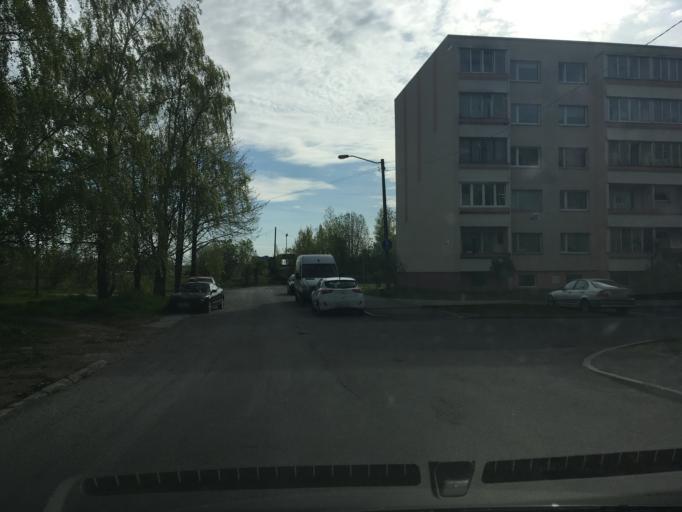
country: EE
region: Harju
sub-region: Tallinna linn
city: Kose
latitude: 59.4430
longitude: 24.8384
